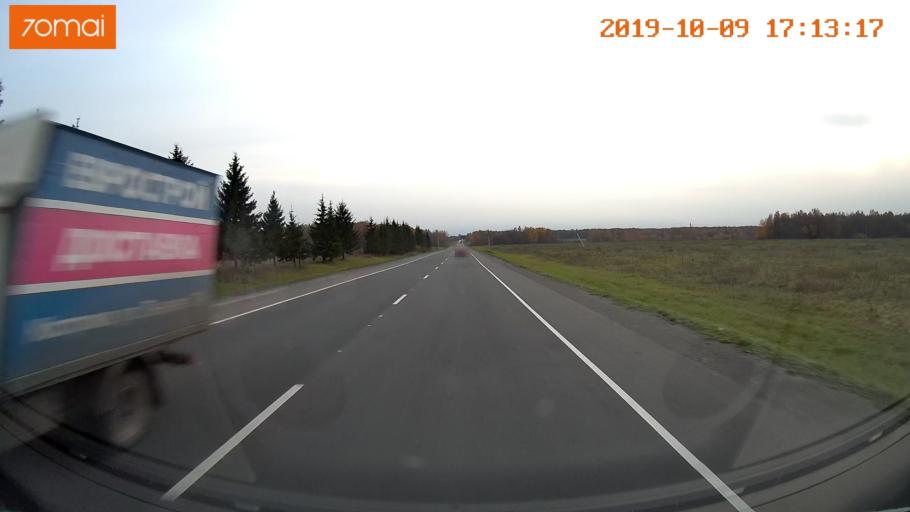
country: RU
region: Ivanovo
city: Privolzhsk
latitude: 57.3174
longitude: 41.2268
